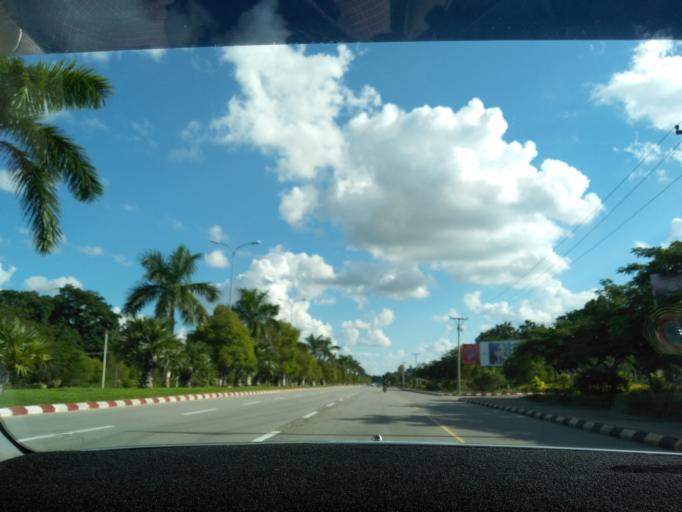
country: MM
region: Mandalay
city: Nay Pyi Taw
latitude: 19.7308
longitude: 96.1110
